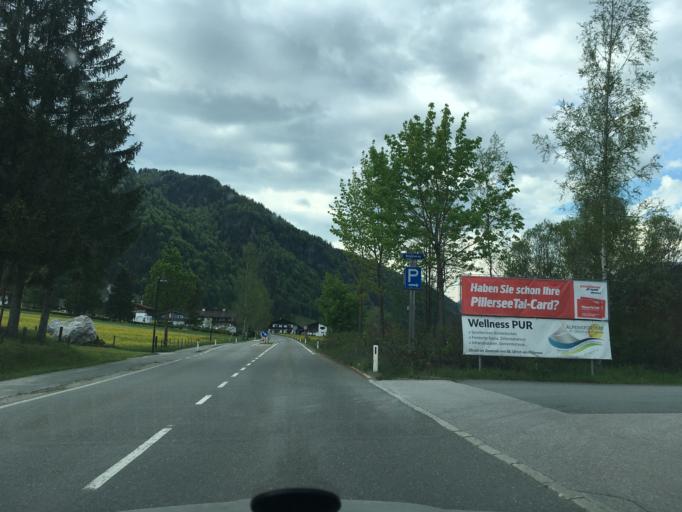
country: AT
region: Tyrol
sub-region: Politischer Bezirk Kitzbuhel
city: Fieberbrunn
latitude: 47.5299
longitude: 12.5732
